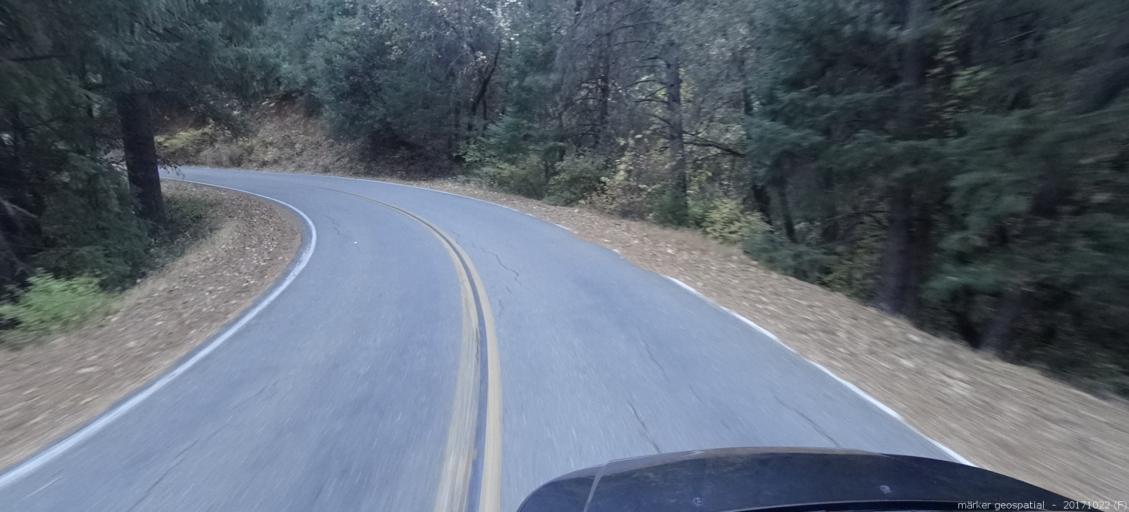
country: US
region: California
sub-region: Shasta County
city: Bella Vista
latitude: 40.8982
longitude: -122.2315
